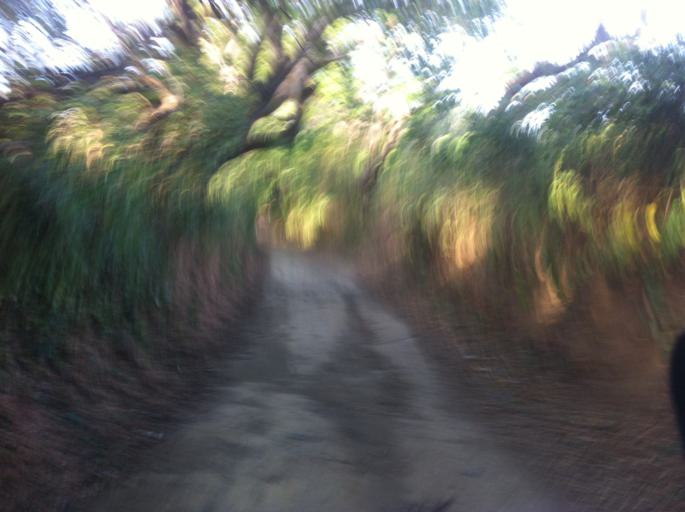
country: NI
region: Managua
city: Managua
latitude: 12.0756
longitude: -86.3098
